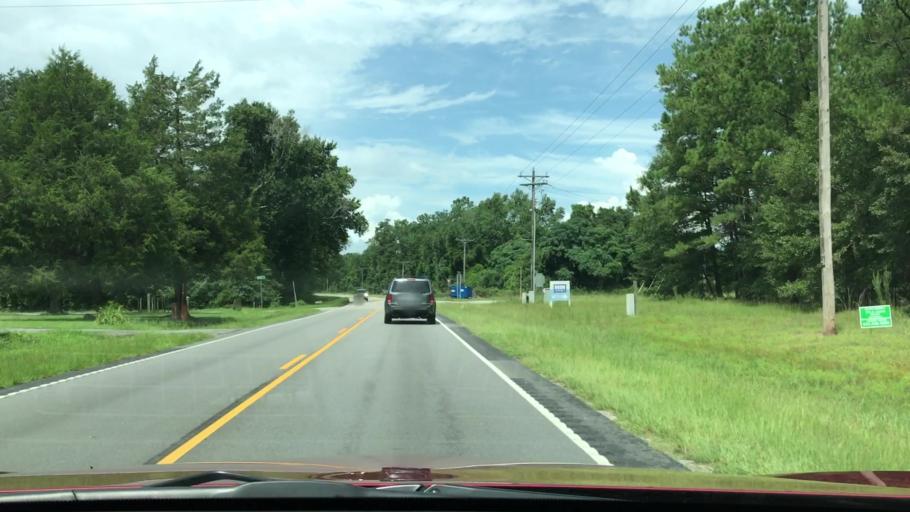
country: US
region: South Carolina
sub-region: Horry County
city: Red Hill
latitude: 33.9037
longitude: -78.9077
